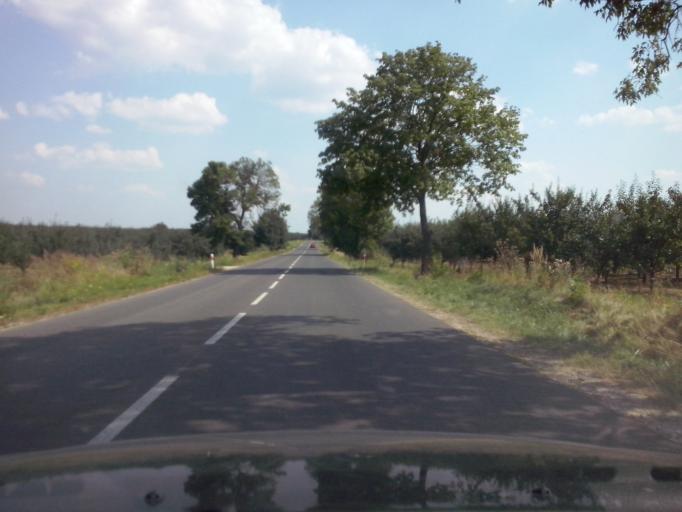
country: PL
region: Swietokrzyskie
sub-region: Powiat staszowski
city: Szydlow
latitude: 50.5873
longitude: 21.0236
